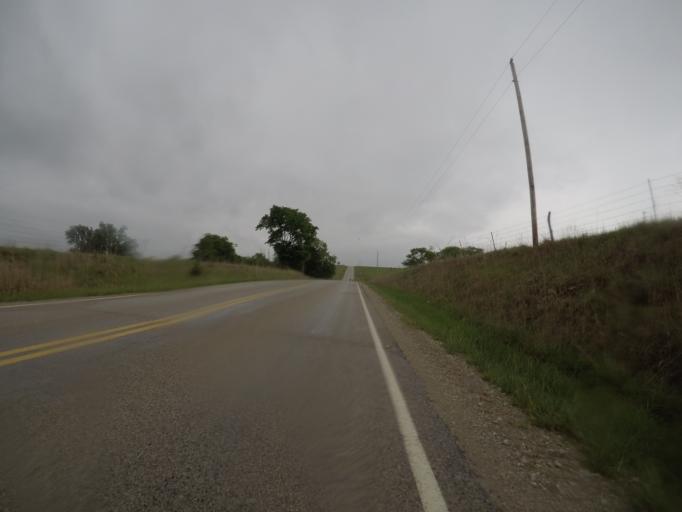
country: US
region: Kansas
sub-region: Pottawatomie County
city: Westmoreland
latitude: 39.4316
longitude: -96.1840
